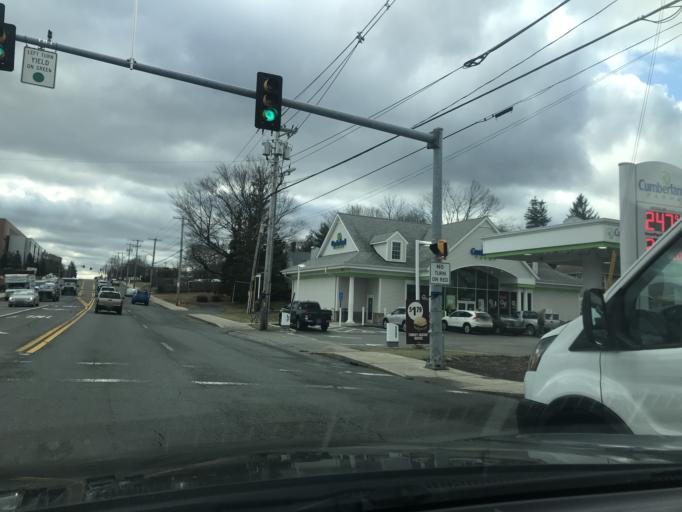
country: US
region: Massachusetts
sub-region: Norfolk County
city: Weymouth
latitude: 42.1797
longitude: -70.9553
